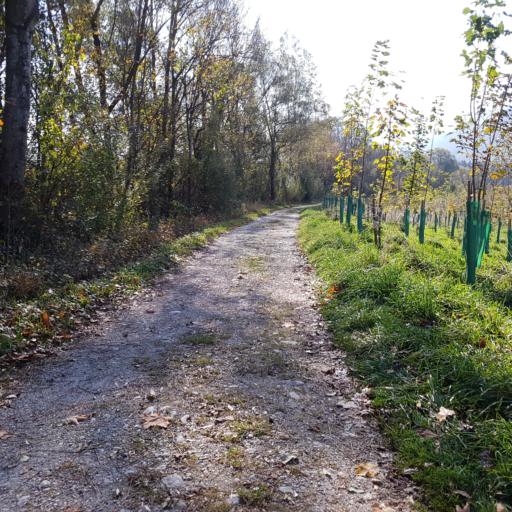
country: AT
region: Salzburg
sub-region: Politischer Bezirk Hallein
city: Adnet
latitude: 47.6688
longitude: 13.1203
